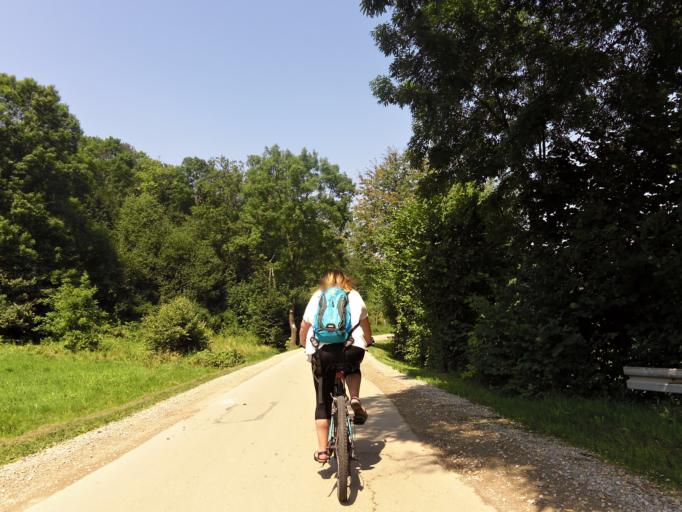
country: PL
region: Silesian Voivodeship
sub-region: Powiat zywiecki
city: Cisiec
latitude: 49.5852
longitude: 19.0932
